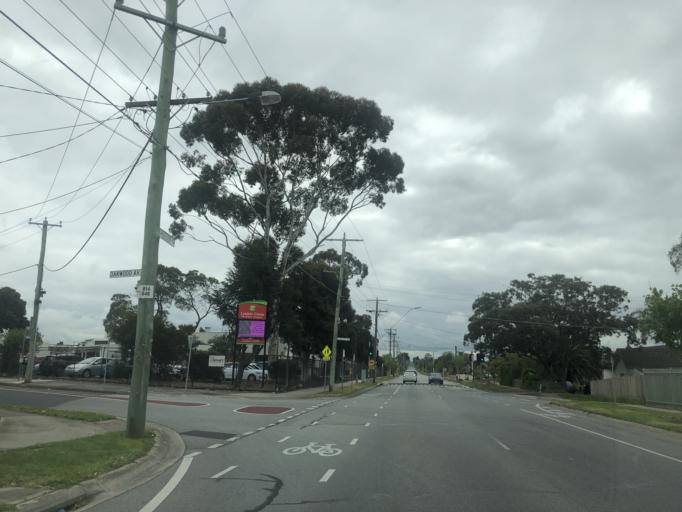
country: AU
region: Victoria
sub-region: Greater Dandenong
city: Dandenong North
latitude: -37.9659
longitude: 145.2056
